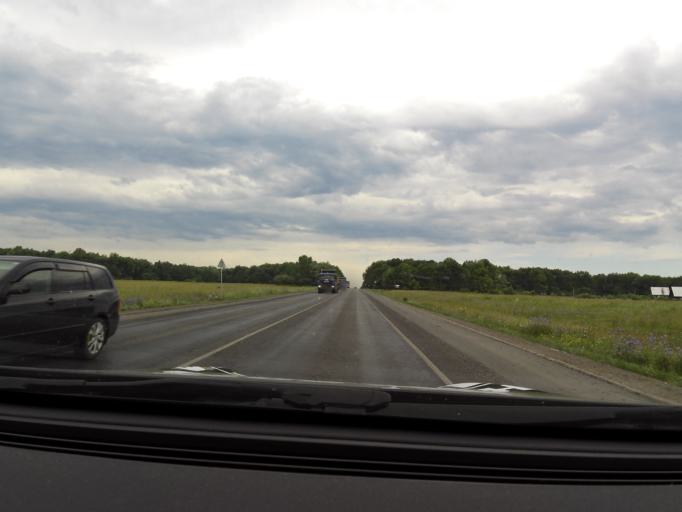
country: RU
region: Bashkortostan
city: Urman
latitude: 54.8175
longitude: 56.8623
